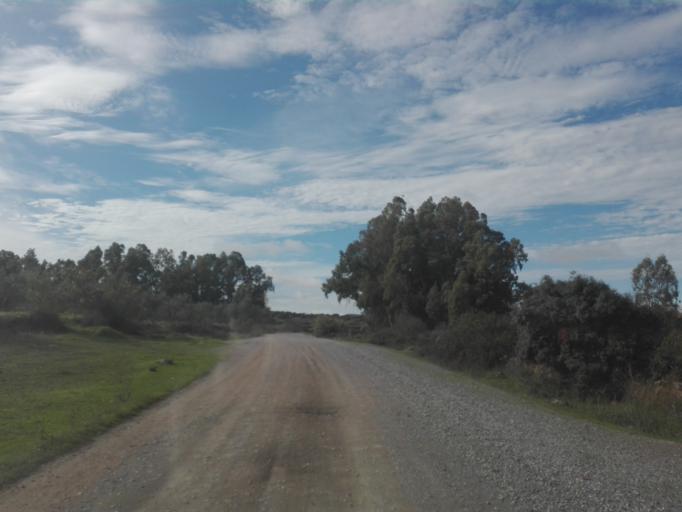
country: ES
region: Extremadura
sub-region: Provincia de Badajoz
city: Villagarcia de la Torre
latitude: 38.2986
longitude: -6.0966
